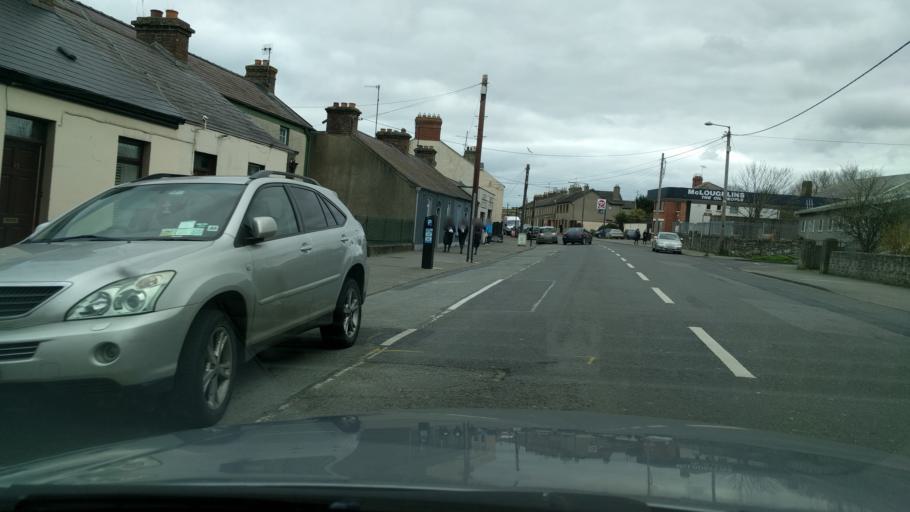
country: IE
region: Leinster
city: Balbriggan
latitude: 53.6128
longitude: -6.1884
